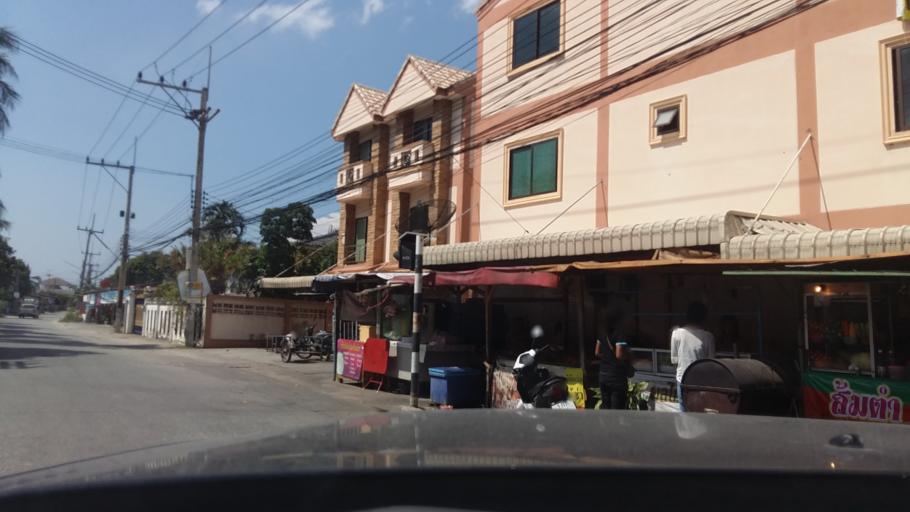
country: TH
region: Chon Buri
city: Chon Buri
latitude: 13.3164
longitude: 100.9305
